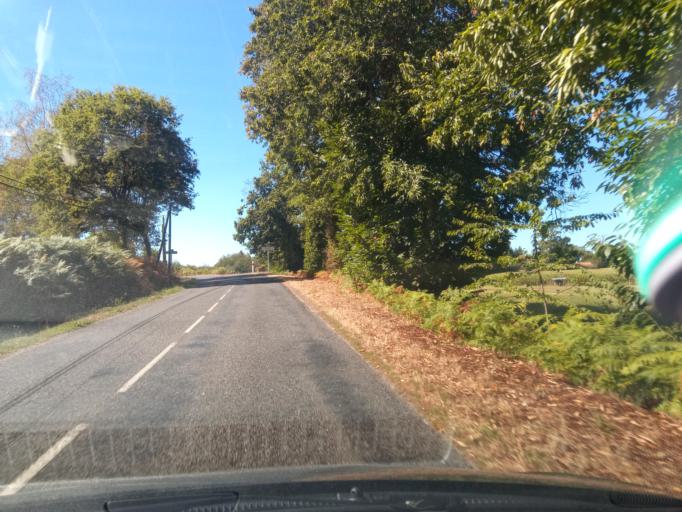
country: FR
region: Limousin
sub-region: Departement de la Haute-Vienne
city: Nantiat
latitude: 46.0795
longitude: 1.2068
